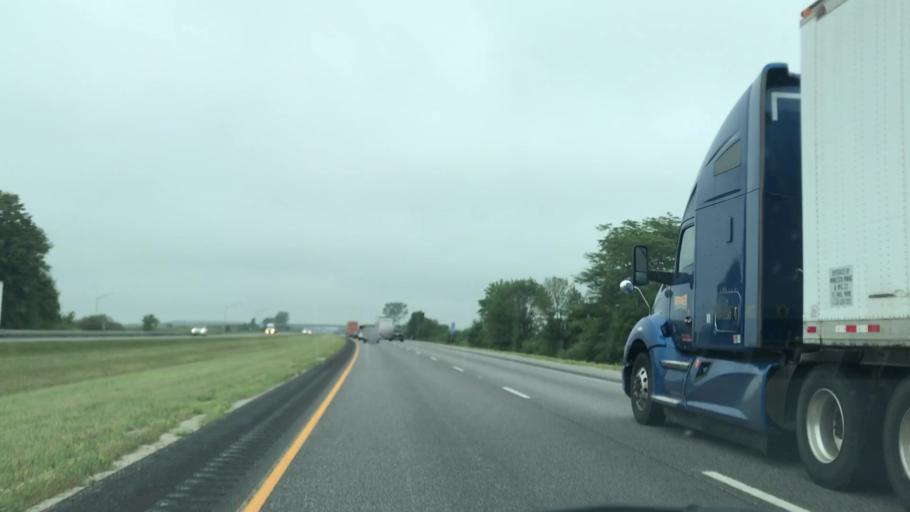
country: US
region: Indiana
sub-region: Boone County
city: Thorntown
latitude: 40.1724
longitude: -86.5506
